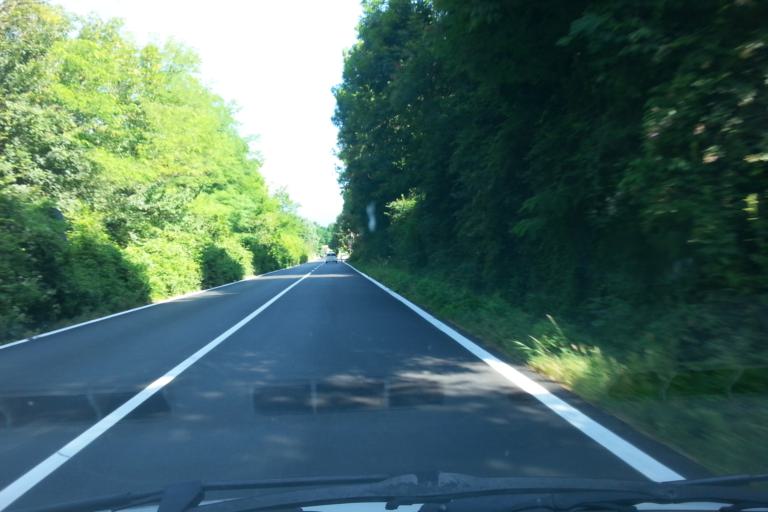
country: IT
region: Piedmont
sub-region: Provincia di Torino
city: Avigliana
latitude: 45.0531
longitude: 7.3967
